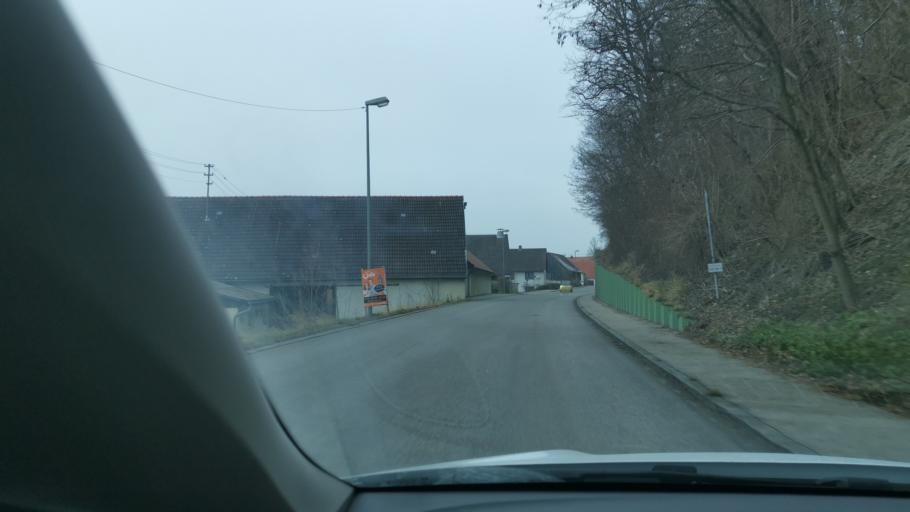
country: DE
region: Bavaria
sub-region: Swabia
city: Rehling
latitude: 48.4921
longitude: 10.9216
